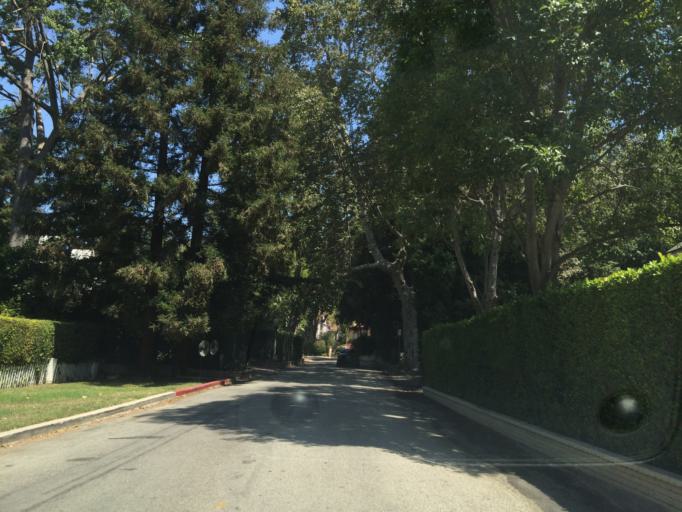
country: US
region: California
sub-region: Los Angeles County
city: Westwood, Los Angeles
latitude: 34.0899
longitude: -118.4469
